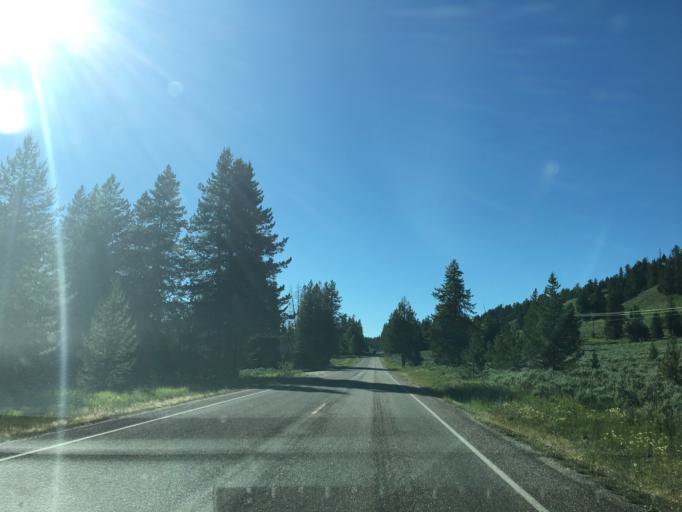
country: US
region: Wyoming
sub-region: Teton County
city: Jackson
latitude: 43.8592
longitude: -110.5297
